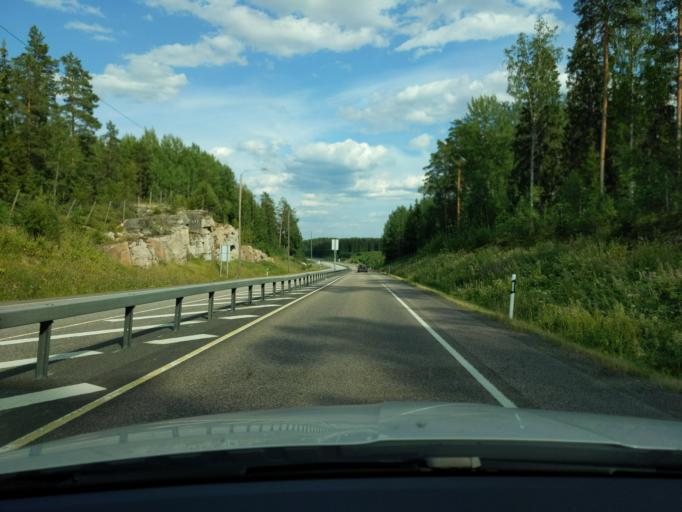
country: FI
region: Kymenlaakso
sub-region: Kouvola
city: Iitti
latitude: 60.9147
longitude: 26.2284
